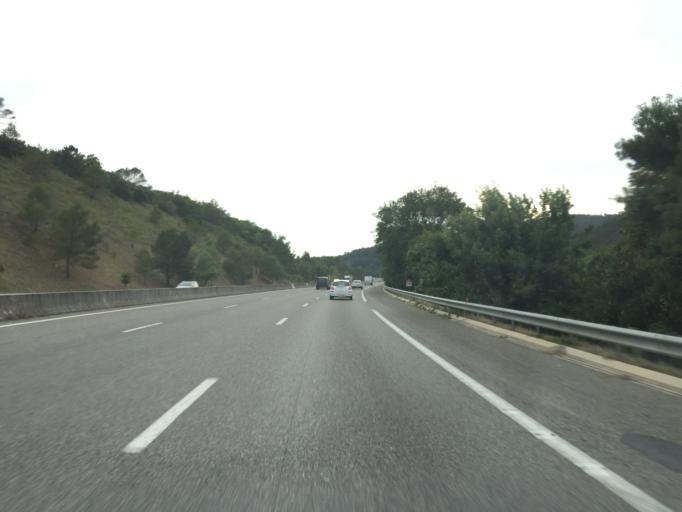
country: FR
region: Provence-Alpes-Cote d'Azur
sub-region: Departement du Var
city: Camps-la-Source
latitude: 43.4179
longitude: 6.1064
